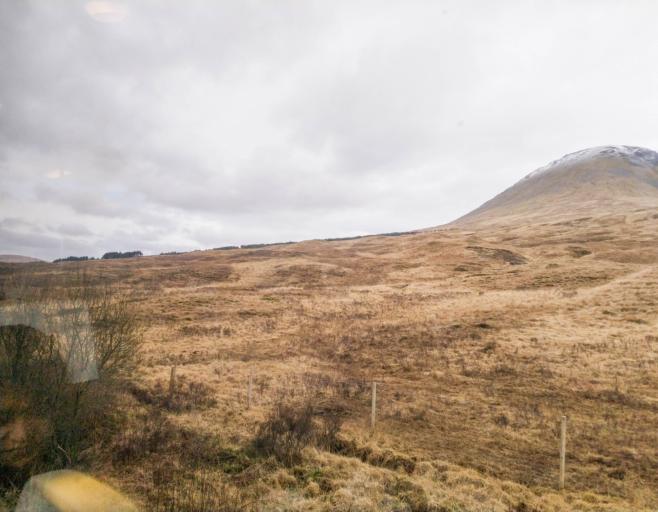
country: GB
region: Scotland
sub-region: Highland
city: Spean Bridge
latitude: 56.5130
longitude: -4.7617
